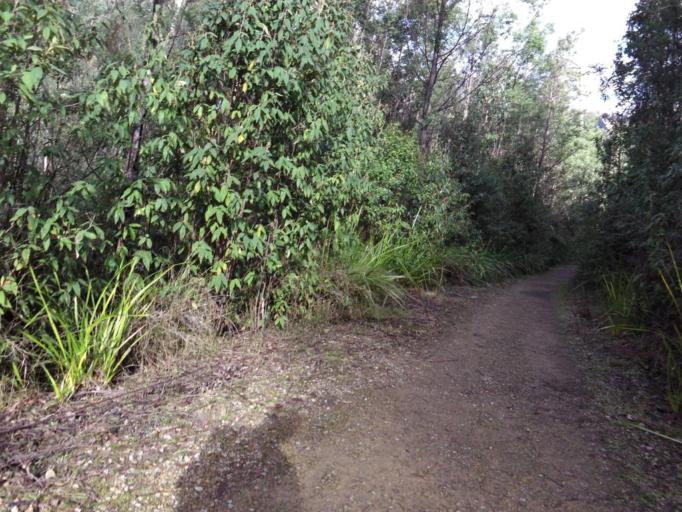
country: AU
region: Victoria
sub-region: Yarra Ranges
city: Millgrove
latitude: -37.5260
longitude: 145.7735
